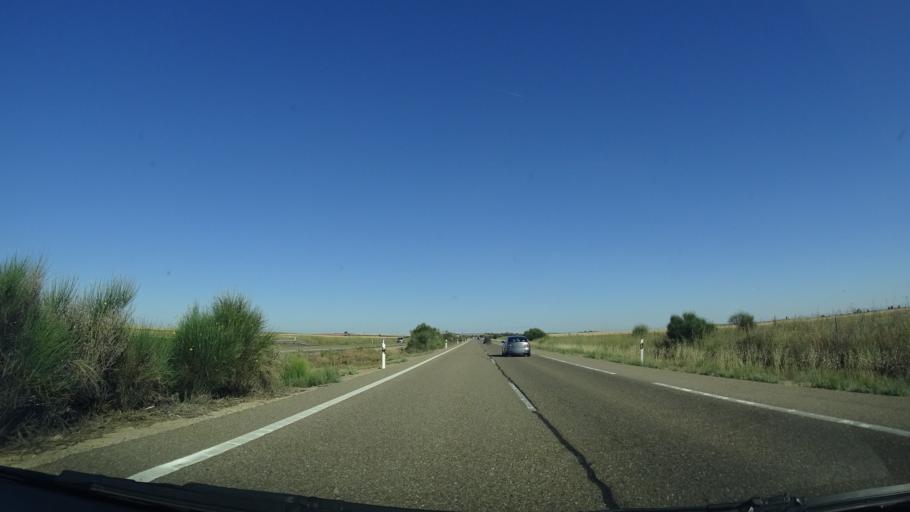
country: ES
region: Castille and Leon
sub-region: Provincia de Valladolid
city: Villardefrades
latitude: 41.7424
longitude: -5.2724
